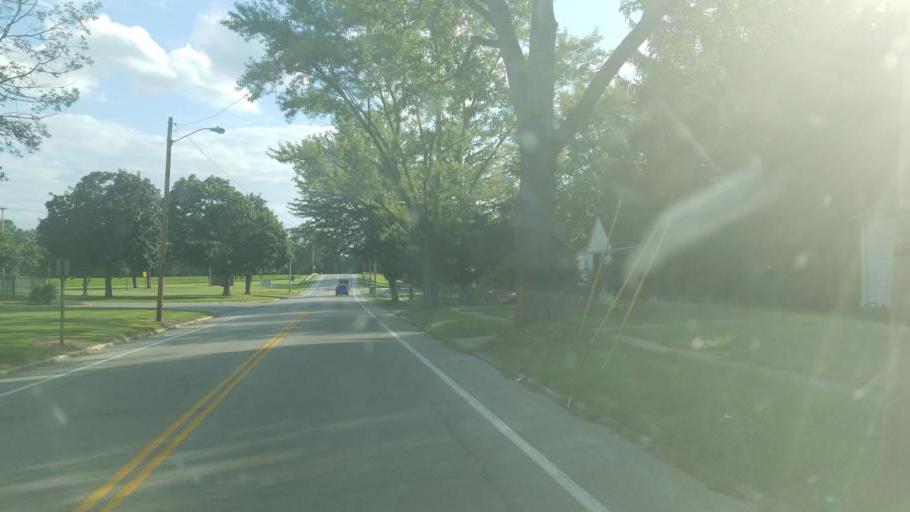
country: US
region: Ohio
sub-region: Sandusky County
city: Ballville
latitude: 41.3345
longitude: -83.1208
